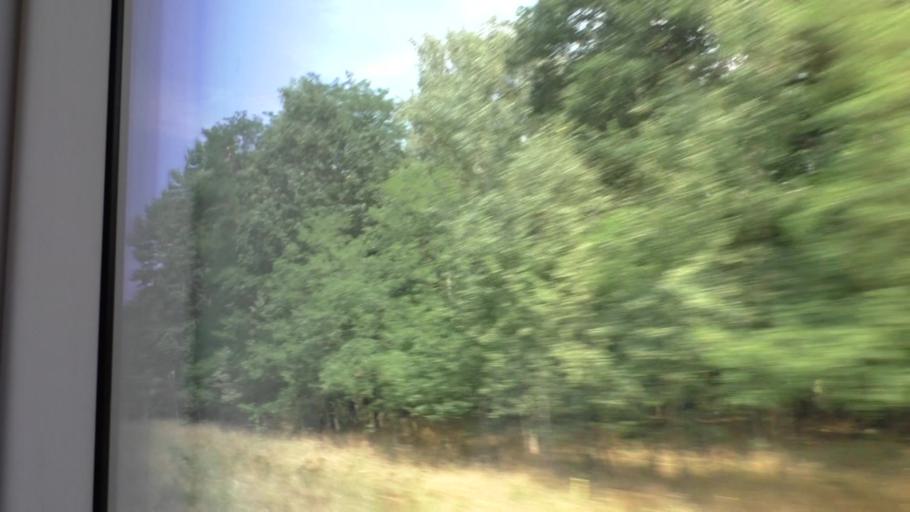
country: DE
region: Brandenburg
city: Mullrose
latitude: 52.2364
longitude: 14.4320
